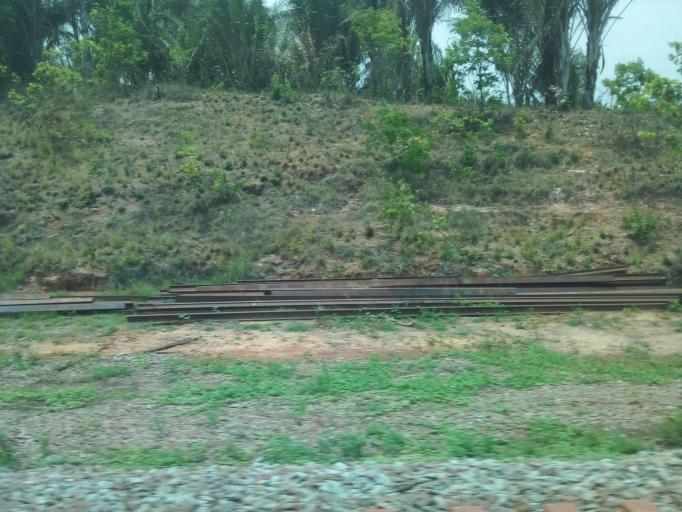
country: BR
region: Maranhao
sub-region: Santa Ines
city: Santa Ines
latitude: -3.7027
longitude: -45.5848
